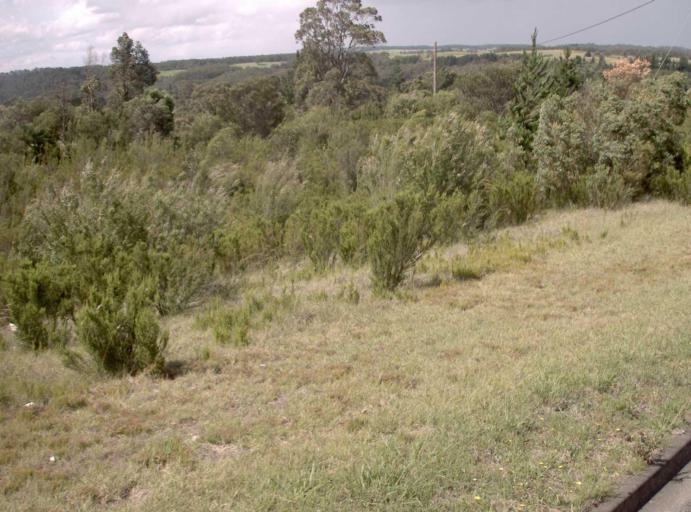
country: AU
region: Victoria
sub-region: Latrobe
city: Moe
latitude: -38.1779
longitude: 146.3328
